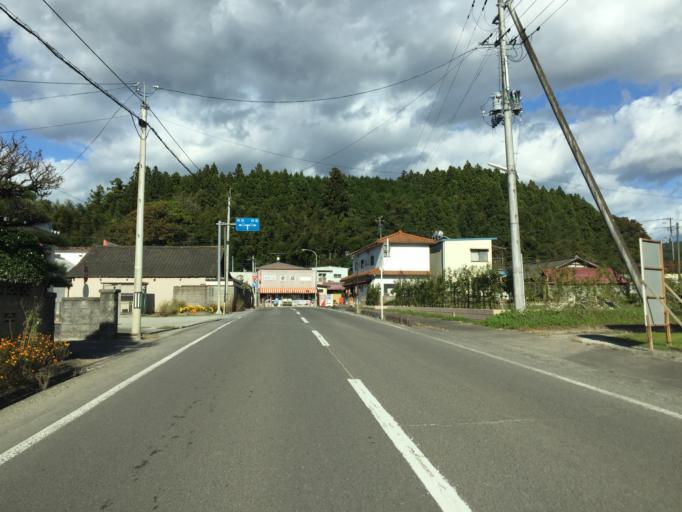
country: JP
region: Miyagi
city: Marumori
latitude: 37.8645
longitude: 140.8276
